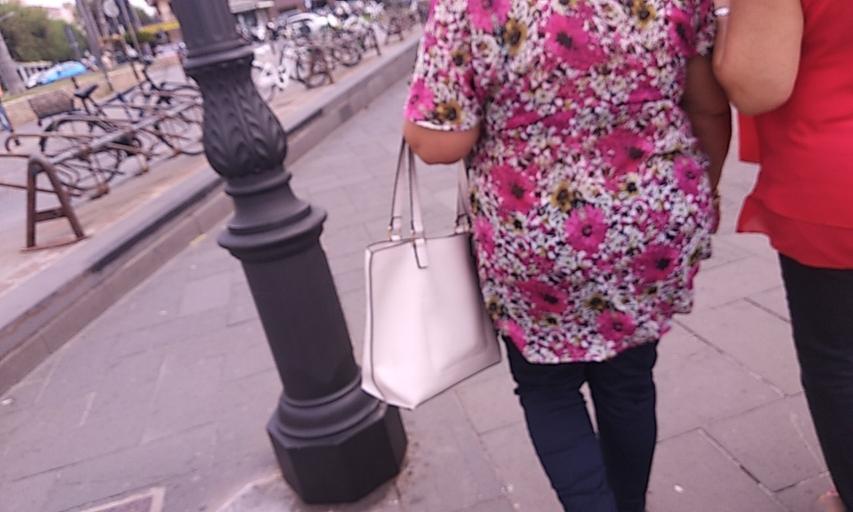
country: IT
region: Sardinia
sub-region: Provincia di Sassari
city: Alghero
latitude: 40.5563
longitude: 8.3150
